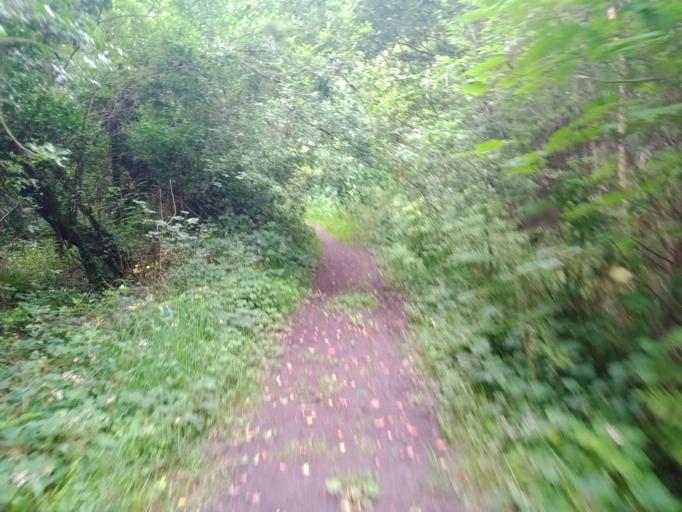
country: IE
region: Leinster
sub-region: Laois
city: Abbeyleix
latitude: 52.8840
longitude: -7.3572
